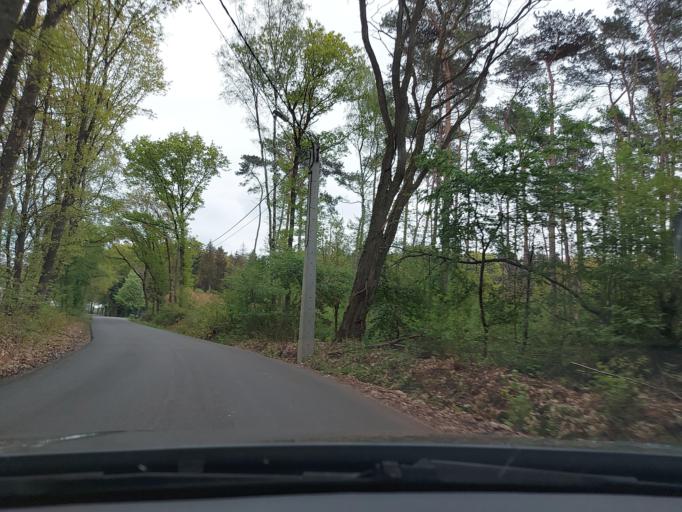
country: BE
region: Flanders
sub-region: Provincie Limburg
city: Zonhoven
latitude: 50.9591
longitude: 5.3794
